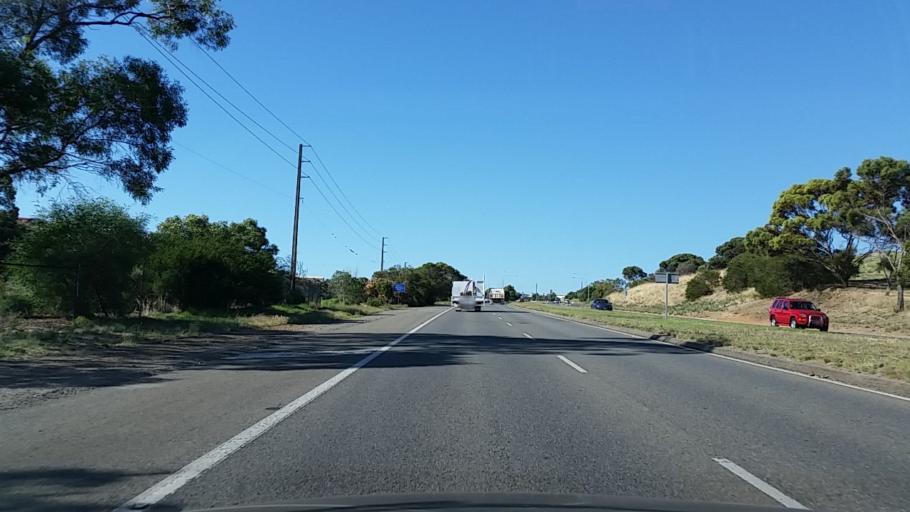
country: AU
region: South Australia
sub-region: Adelaide
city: Port Noarlunga
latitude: -35.1227
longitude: 138.4874
